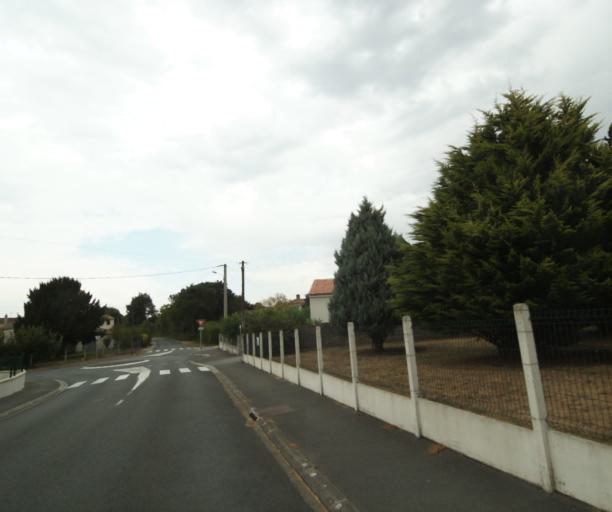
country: FR
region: Poitou-Charentes
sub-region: Departement de la Charente-Maritime
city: Tonnay-Charente
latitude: 45.9478
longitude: -0.8869
